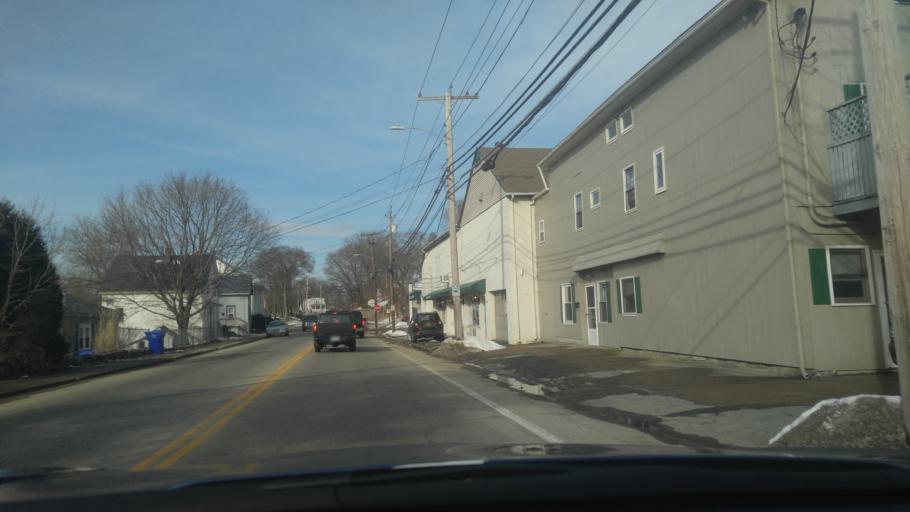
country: US
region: Rhode Island
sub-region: Kent County
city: West Warwick
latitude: 41.6912
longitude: -71.5212
